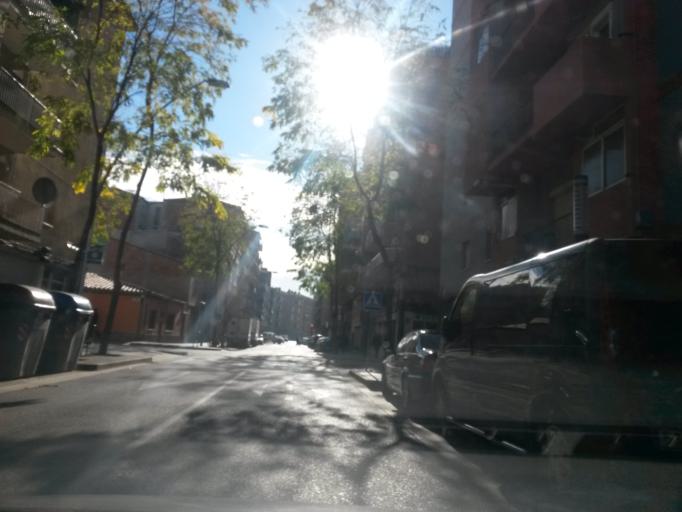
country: ES
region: Catalonia
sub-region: Provincia de Girona
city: Salt
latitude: 41.9754
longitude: 2.8028
